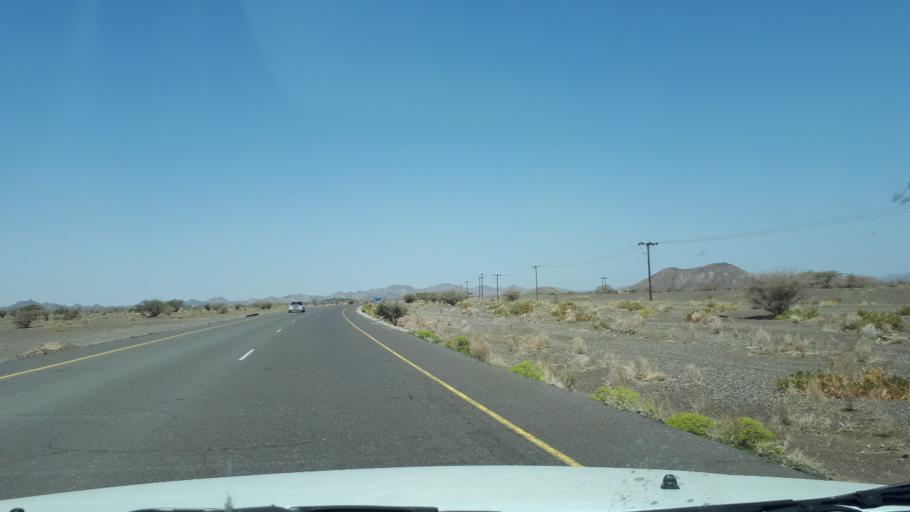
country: OM
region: Ash Sharqiyah
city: Ibra'
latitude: 22.6174
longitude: 58.4204
